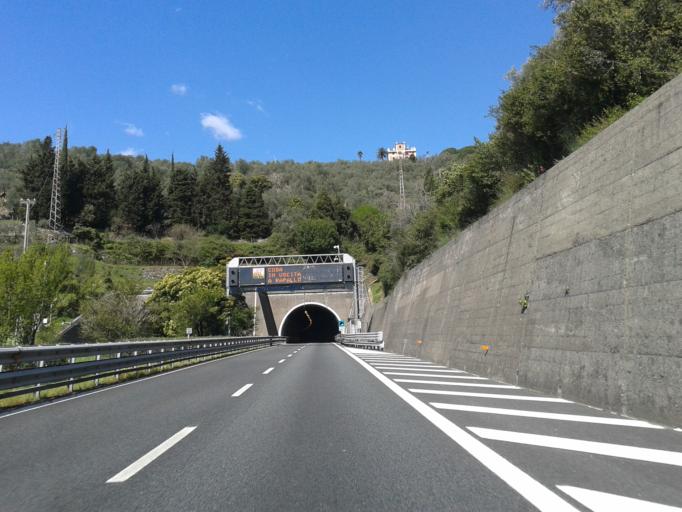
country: IT
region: Liguria
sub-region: Provincia di Genova
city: Chiavari
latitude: 44.3236
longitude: 9.3349
